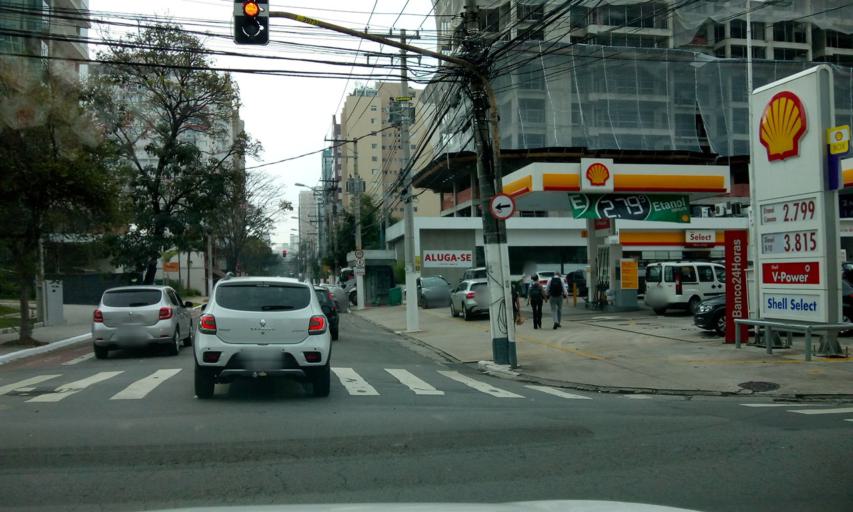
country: BR
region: Sao Paulo
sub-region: Sao Paulo
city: Sao Paulo
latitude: -23.6102
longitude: -46.6636
